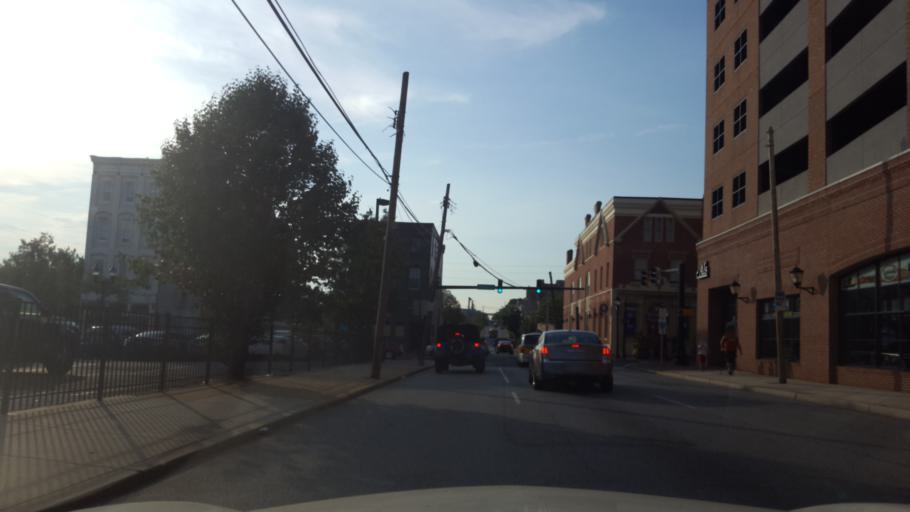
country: US
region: Delaware
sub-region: New Castle County
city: Wilmington
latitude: 39.7386
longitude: -75.5520
